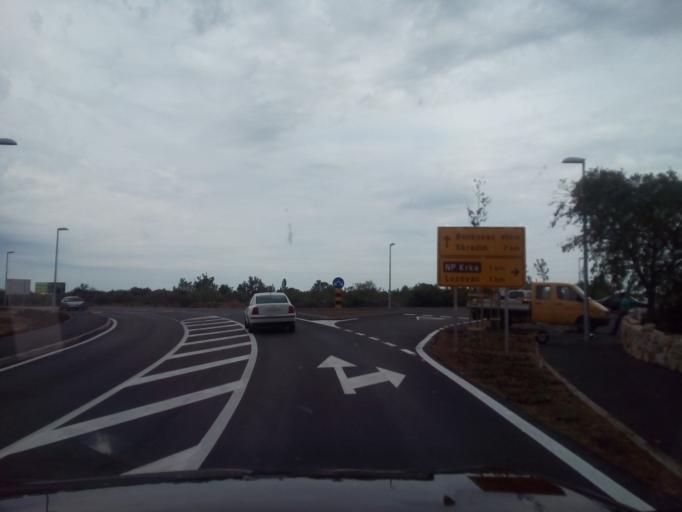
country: HR
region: Sibensko-Kniniska
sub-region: Grad Sibenik
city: Sibenik
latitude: 43.7839
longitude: 15.9665
